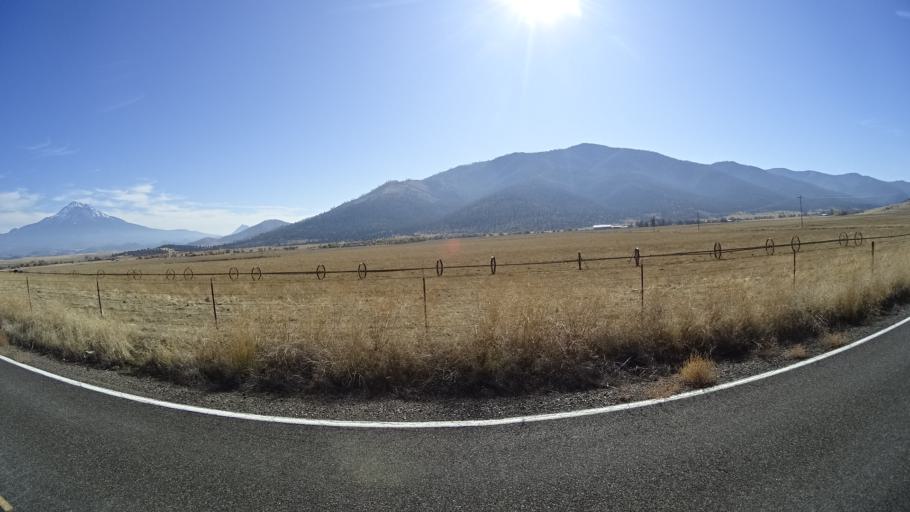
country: US
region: California
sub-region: Siskiyou County
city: Weed
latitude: 41.5065
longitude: -122.5407
